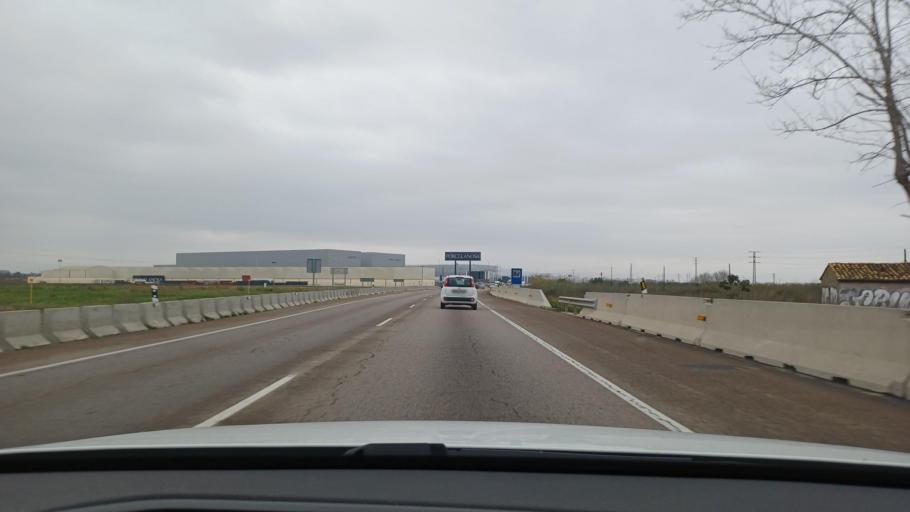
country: ES
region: Valencia
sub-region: Provincia de Castello
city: Alquerias del Nino Perdido
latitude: 39.9072
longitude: -0.1157
